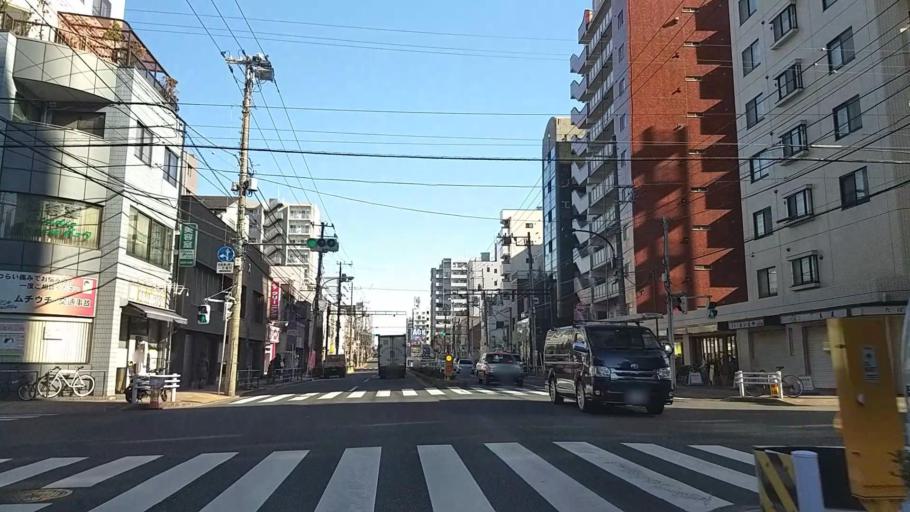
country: JP
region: Tokyo
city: Urayasu
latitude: 35.6885
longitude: 139.8074
